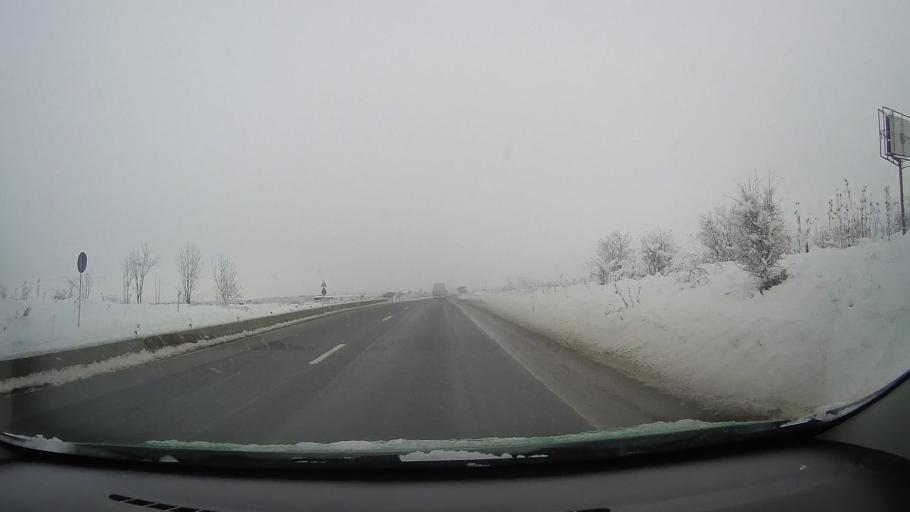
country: RO
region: Sibiu
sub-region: Comuna Cristian
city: Cristian
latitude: 45.7889
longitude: 24.0631
